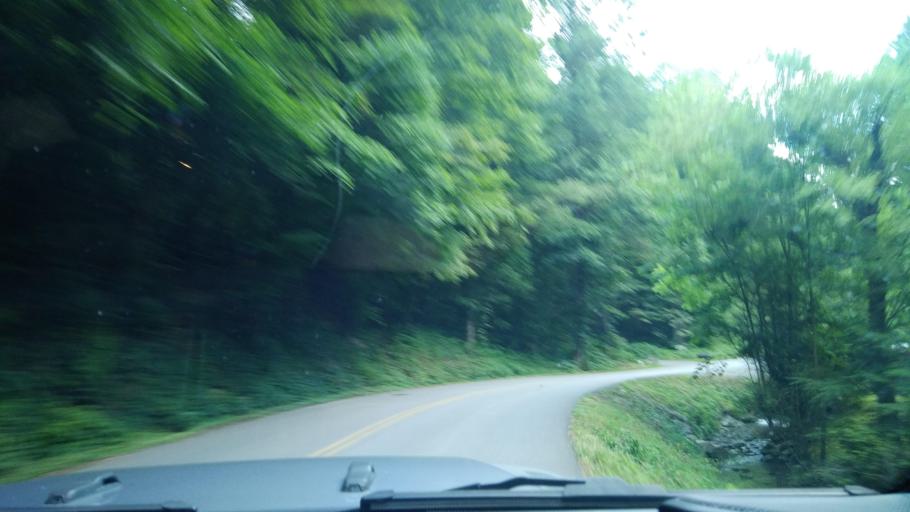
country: US
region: Tennessee
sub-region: Sevier County
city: Gatlinburg
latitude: 35.7279
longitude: -83.4900
